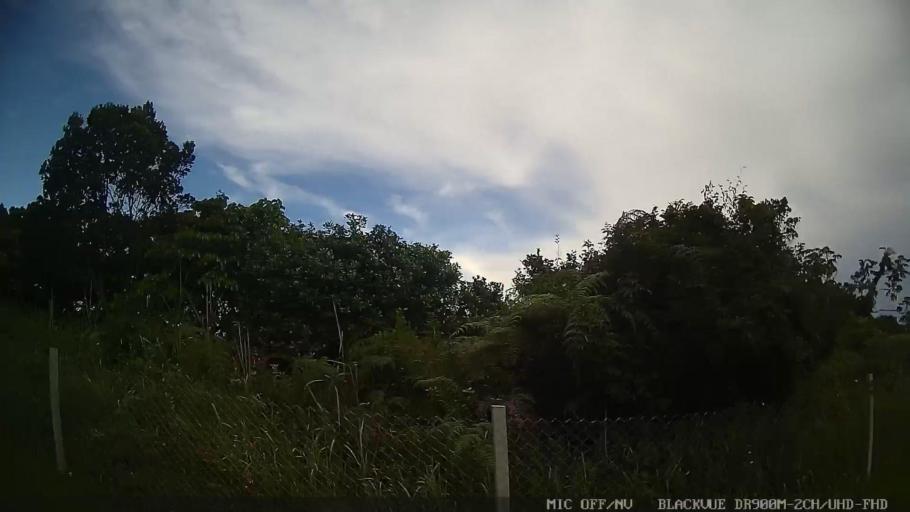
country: BR
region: Sao Paulo
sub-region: Iguape
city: Iguape
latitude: -24.6497
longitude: -47.3991
